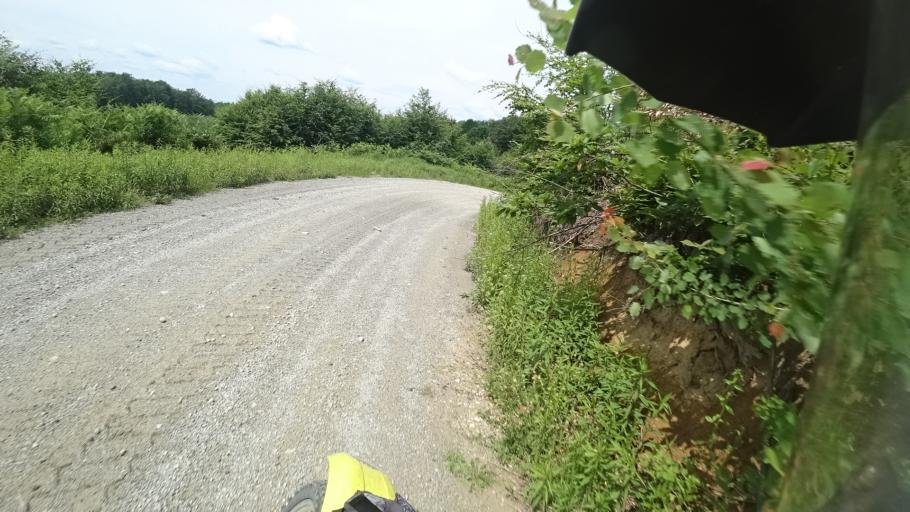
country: HR
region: Karlovacka
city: Vojnic
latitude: 45.2842
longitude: 15.7557
